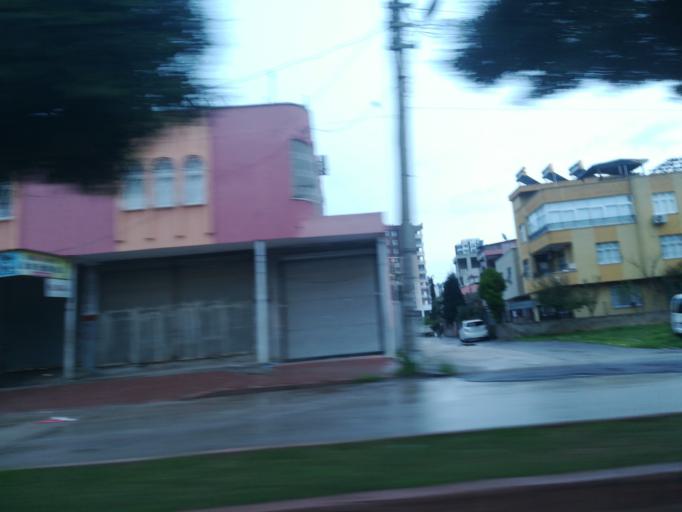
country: TR
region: Adana
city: Seyhan
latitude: 37.0218
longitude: 35.2722
